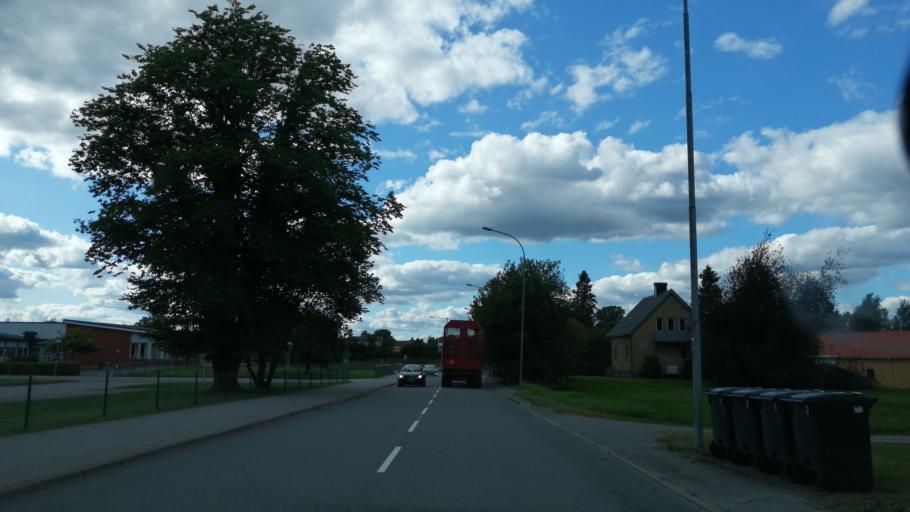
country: SE
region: Joenkoeping
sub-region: Gislaveds Kommun
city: Reftele
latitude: 57.1718
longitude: 13.6010
